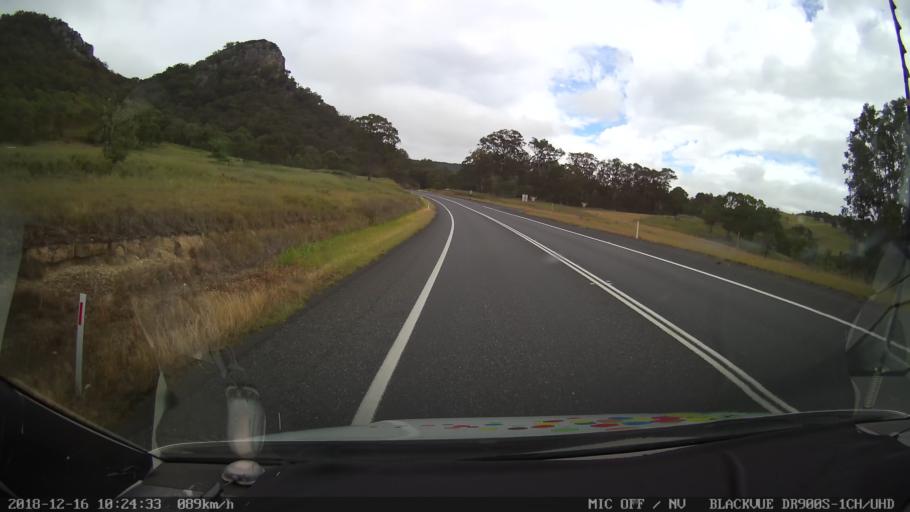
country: AU
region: New South Wales
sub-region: Tenterfield Municipality
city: Carrolls Creek
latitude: -29.1690
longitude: 152.0059
